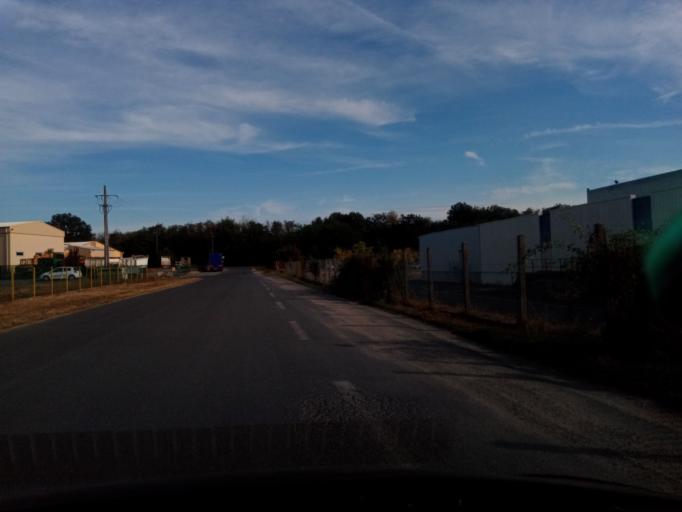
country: FR
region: Poitou-Charentes
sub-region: Departement de la Vienne
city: Saulge
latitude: 46.4022
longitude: 0.8902
